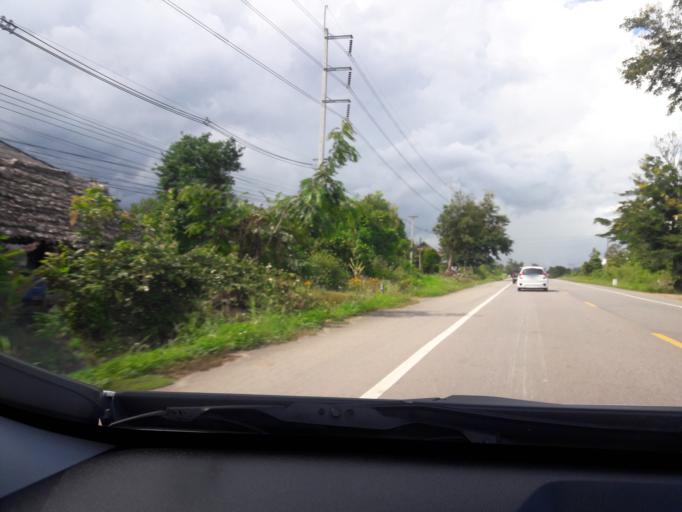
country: TH
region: Mae Hong Son
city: Mae Hi
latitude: 19.3290
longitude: 98.4353
